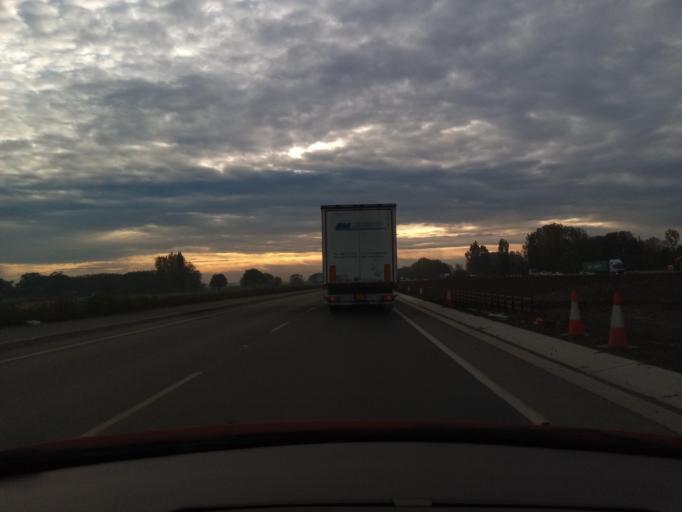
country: GB
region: England
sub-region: Cambridgeshire
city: Girton
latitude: 52.2540
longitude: 0.0326
